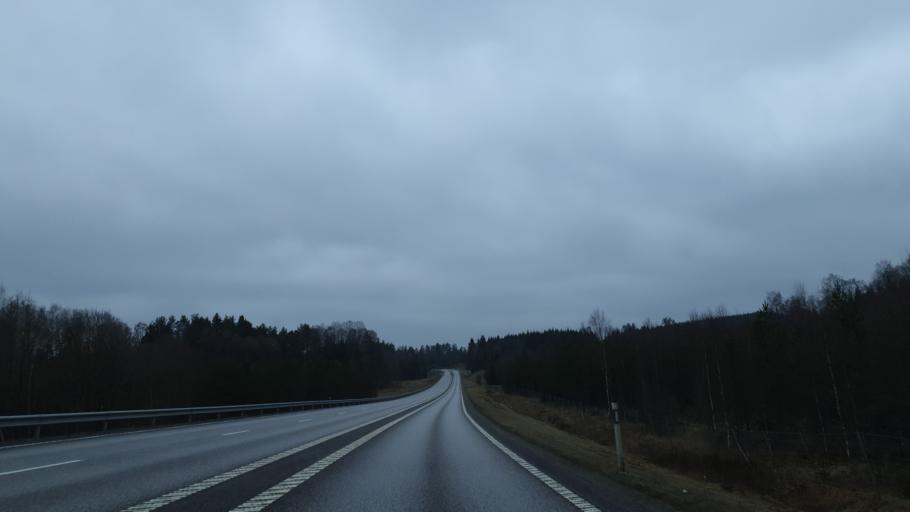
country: SE
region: Vaestra Goetaland
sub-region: Boras Kommun
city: Viskafors
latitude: 57.6005
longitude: 12.8725
